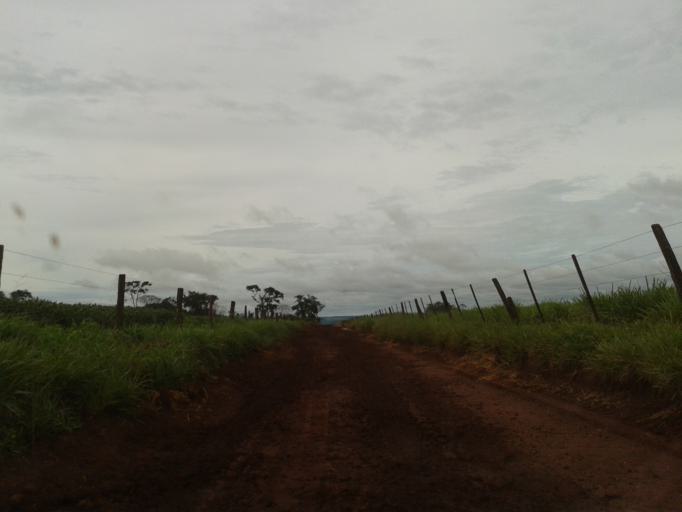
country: BR
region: Minas Gerais
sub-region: Capinopolis
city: Capinopolis
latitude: -18.7484
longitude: -49.7825
